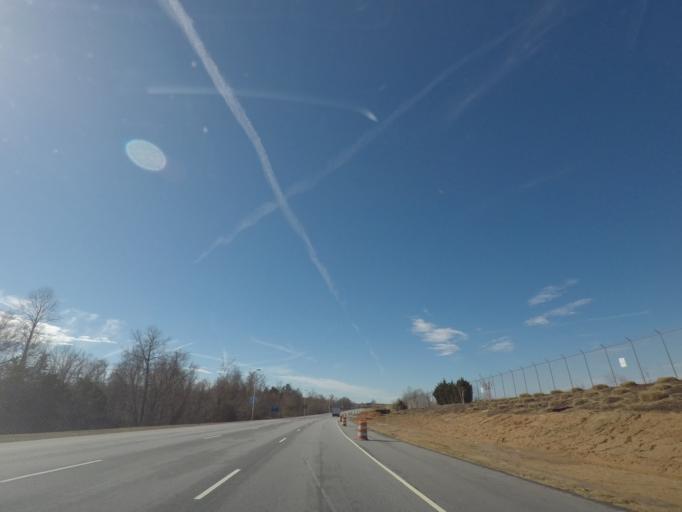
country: US
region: North Carolina
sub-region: Guilford County
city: Oak Ridge
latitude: 36.1120
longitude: -79.9378
